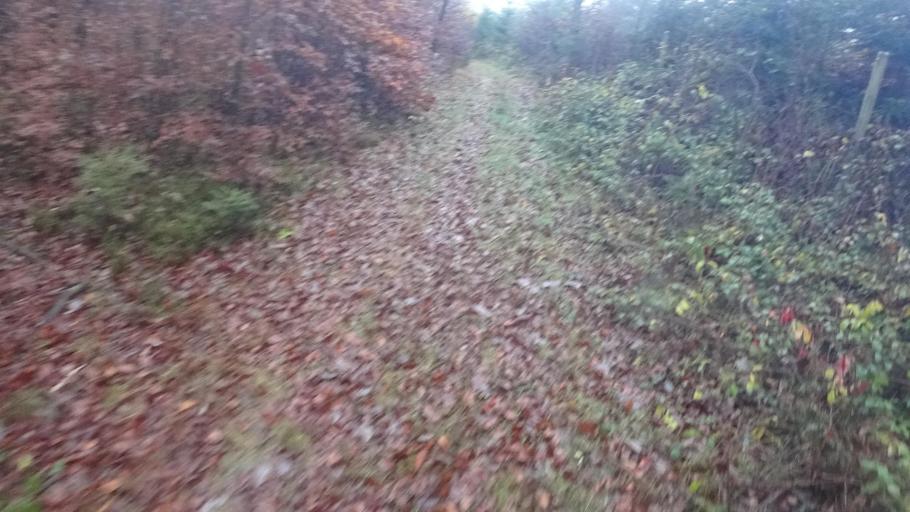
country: DE
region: Rheinland-Pfalz
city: Wiebelsheim
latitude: 50.0729
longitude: 7.6499
